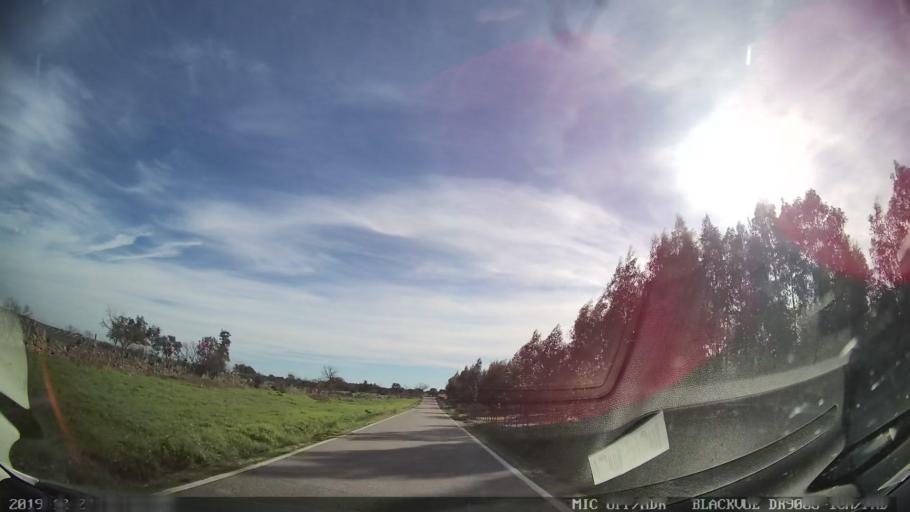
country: PT
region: Portalegre
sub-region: Nisa
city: Nisa
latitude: 39.4902
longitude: -7.7419
